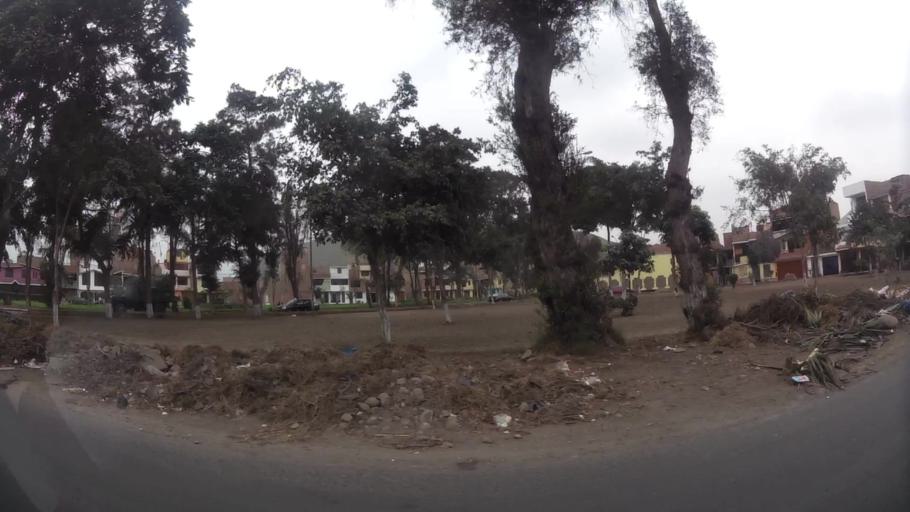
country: PE
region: Lima
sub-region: Lima
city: Independencia
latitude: -11.9377
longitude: -77.0845
